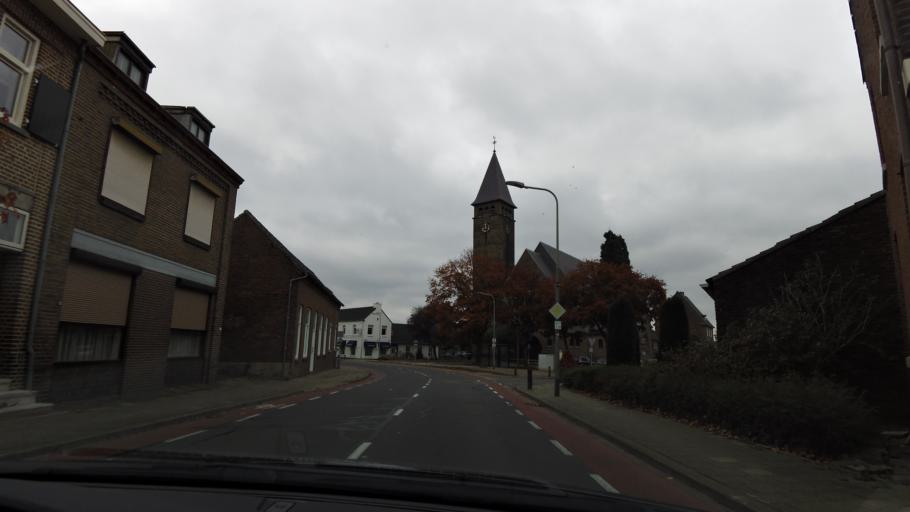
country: NL
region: Limburg
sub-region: Gemeente Schinnen
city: Puth
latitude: 50.9551
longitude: 5.8704
